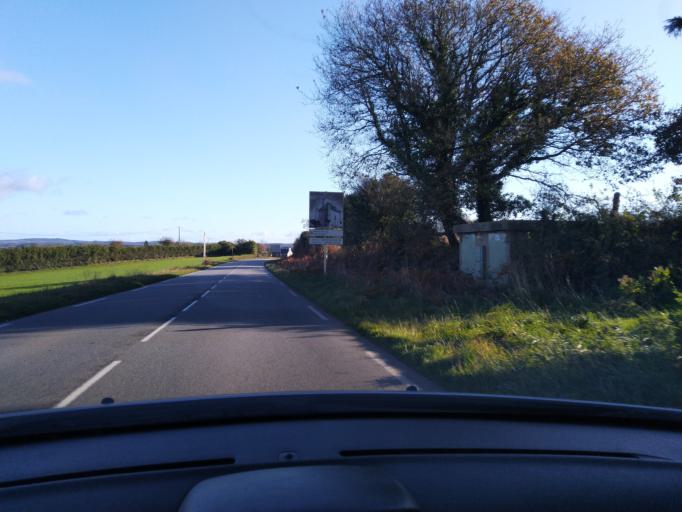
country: FR
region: Brittany
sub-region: Departement du Finistere
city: Guerlesquin
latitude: 48.5252
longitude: -3.5939
